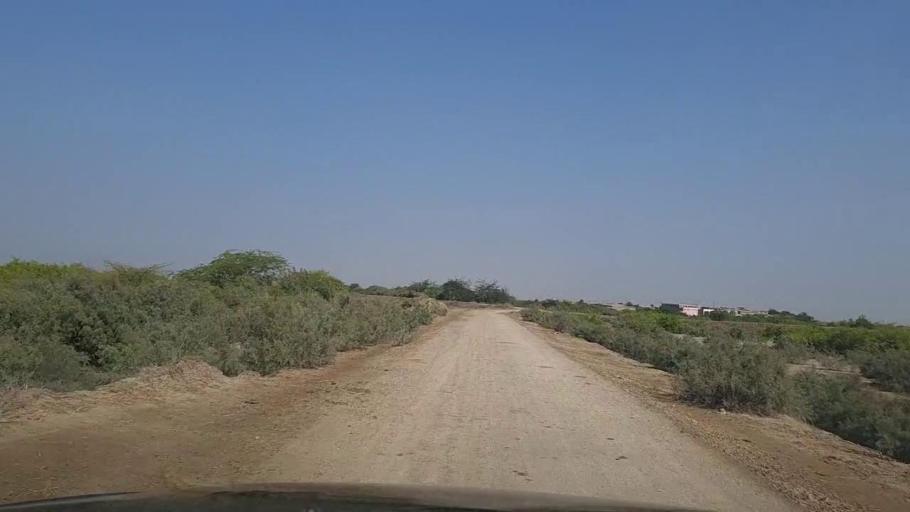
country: PK
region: Sindh
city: Thatta
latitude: 24.6460
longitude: 67.8167
